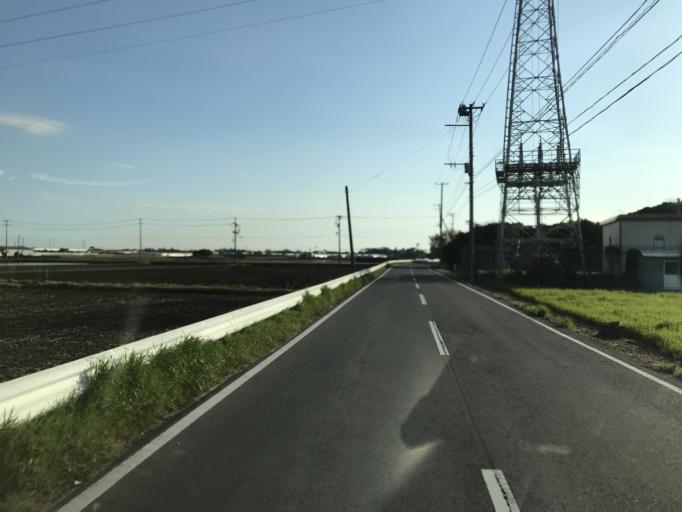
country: JP
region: Chiba
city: Yokaichiba
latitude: 35.6718
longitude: 140.5862
